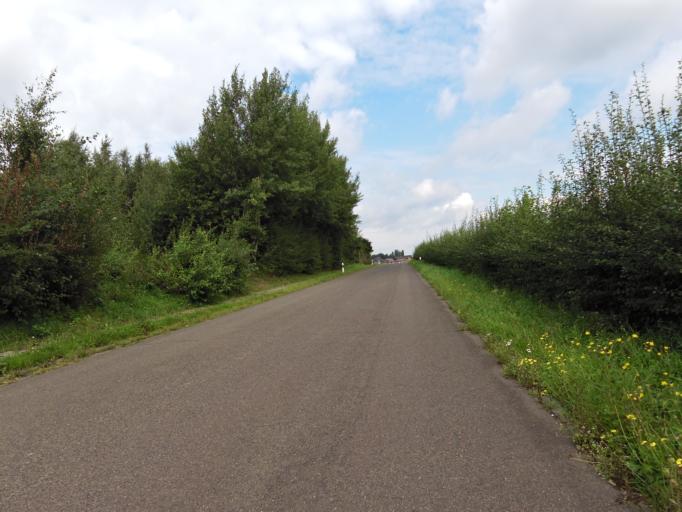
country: DE
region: North Rhine-Westphalia
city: Geilenkirchen
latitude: 50.9609
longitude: 6.0742
